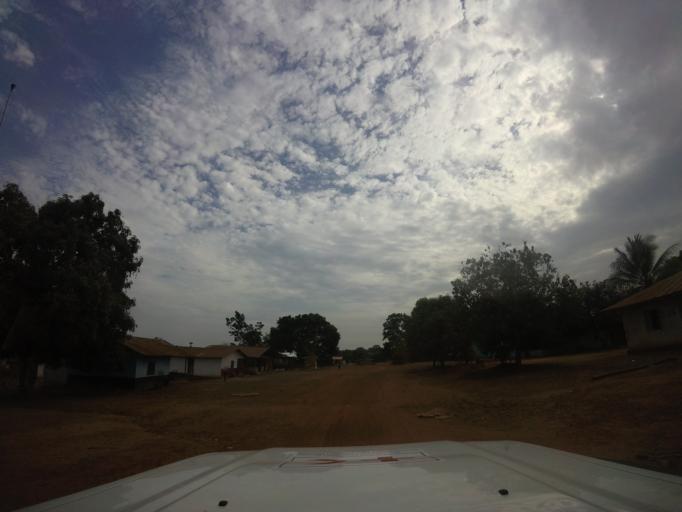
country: LR
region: Grand Cape Mount
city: Robertsport
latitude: 6.9723
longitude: -11.3098
